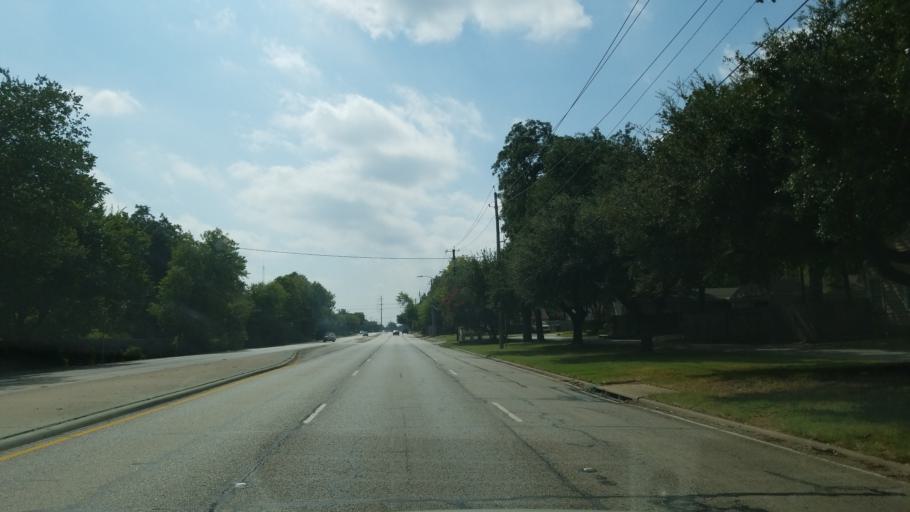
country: US
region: Texas
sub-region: Dallas County
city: Garland
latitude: 32.9022
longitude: -96.6488
